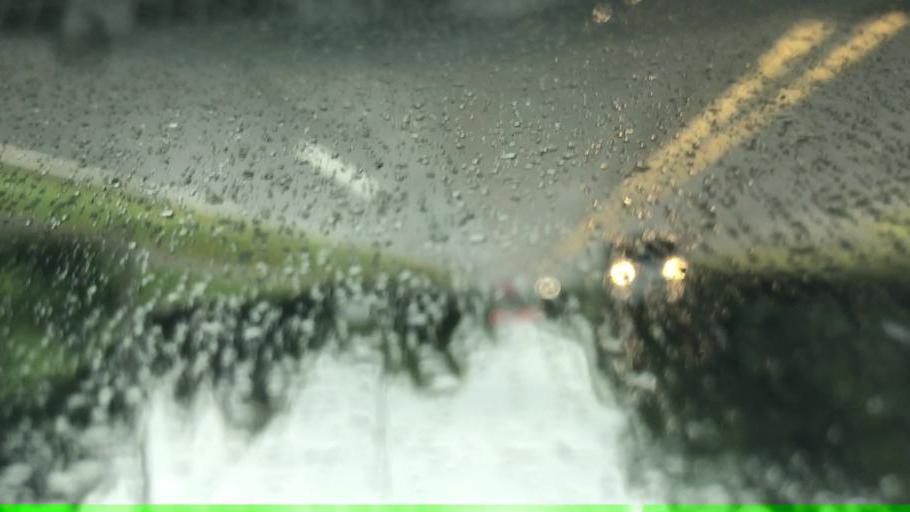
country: US
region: Michigan
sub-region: Oakland County
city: Lake Orion
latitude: 42.7365
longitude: -83.2904
